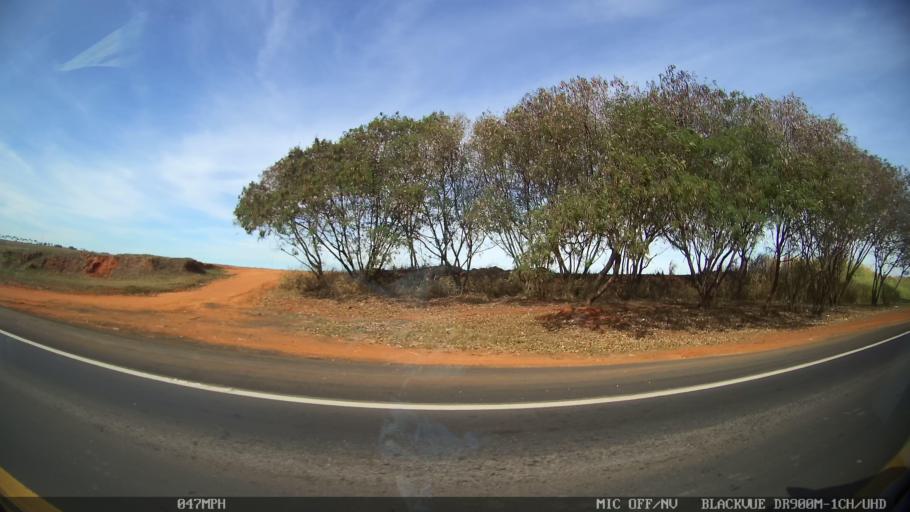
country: BR
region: Sao Paulo
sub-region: Rio Das Pedras
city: Rio das Pedras
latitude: -22.7958
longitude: -47.5957
